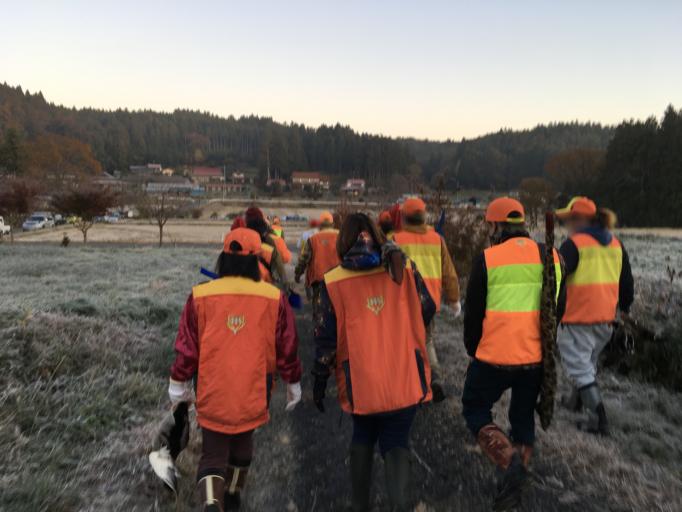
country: JP
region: Iwate
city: Ichinoseki
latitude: 38.8053
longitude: 141.1536
